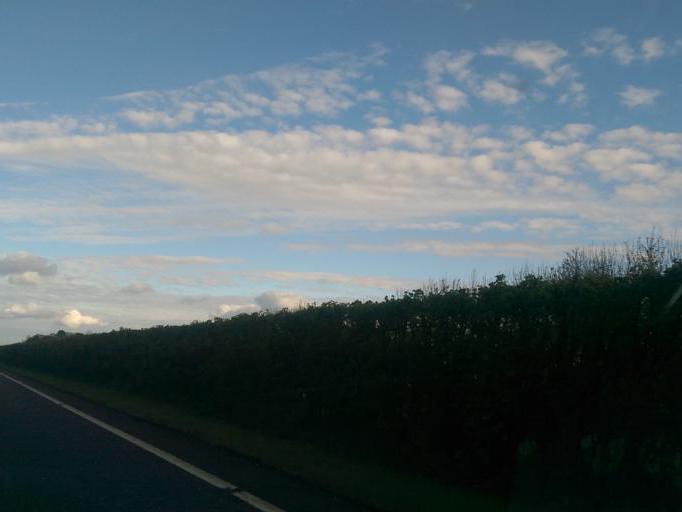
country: IE
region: Leinster
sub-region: Kildare
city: Kilcock
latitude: 53.3809
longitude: -6.6516
